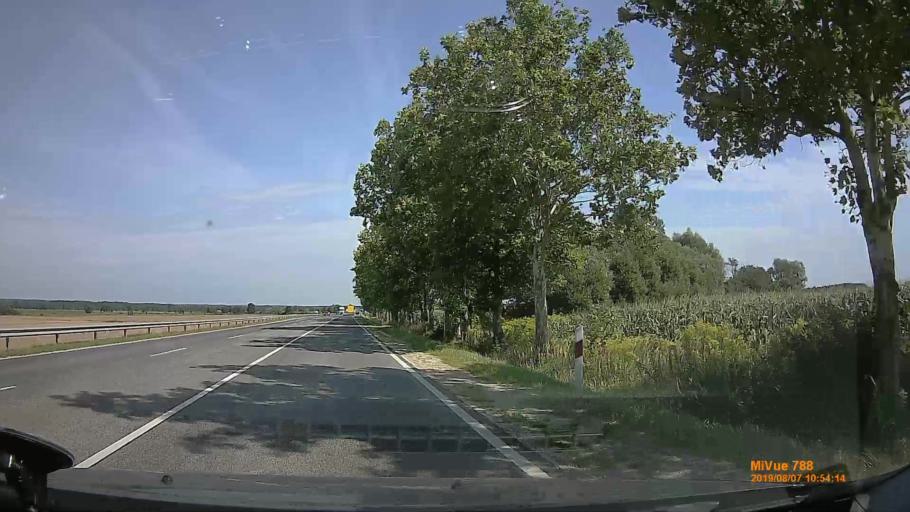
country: SI
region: Lendava-Lendva
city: Lendava
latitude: 46.6069
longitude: 16.4636
